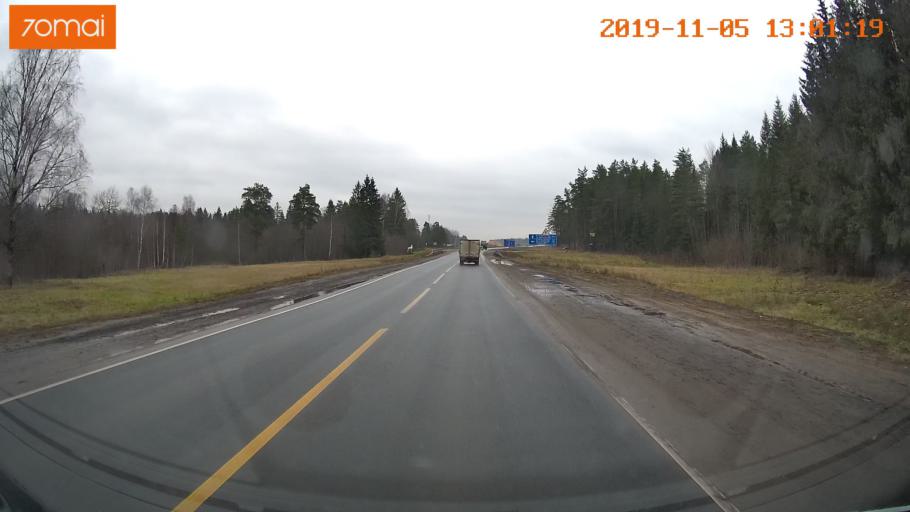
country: RU
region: Ivanovo
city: Kokhma
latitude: 56.9097
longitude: 41.1598
